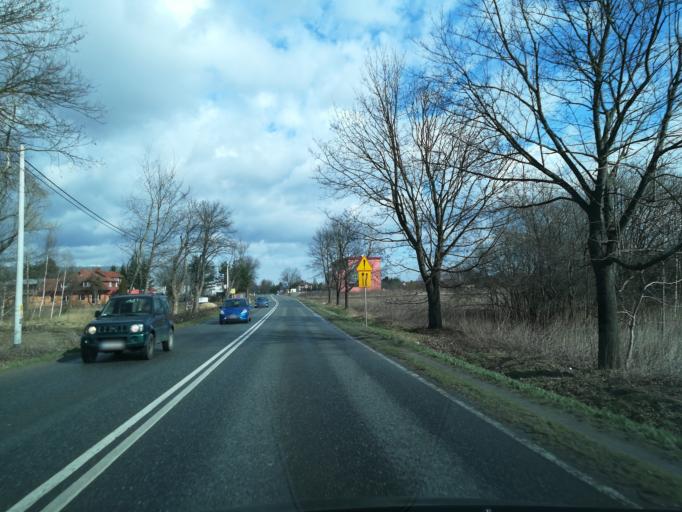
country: PL
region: Lesser Poland Voivodeship
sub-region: Powiat krakowski
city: Kryspinow
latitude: 50.0560
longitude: 19.8022
